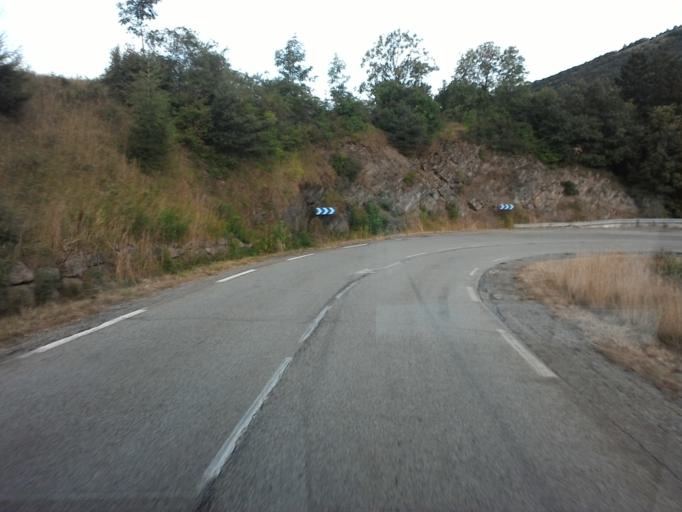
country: FR
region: Rhone-Alpes
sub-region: Departement de l'Isere
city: La Mure
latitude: 44.8320
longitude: 5.9113
